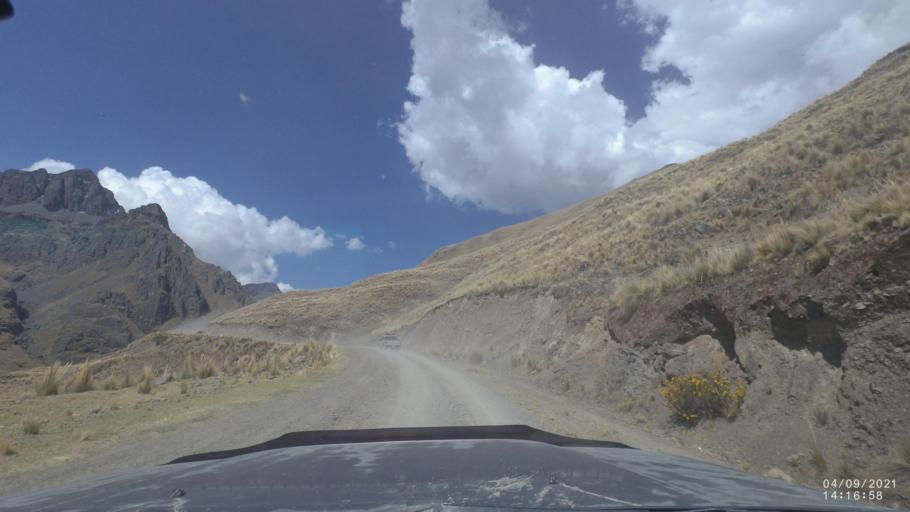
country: BO
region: Cochabamba
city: Sipe Sipe
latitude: -17.2308
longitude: -66.4370
